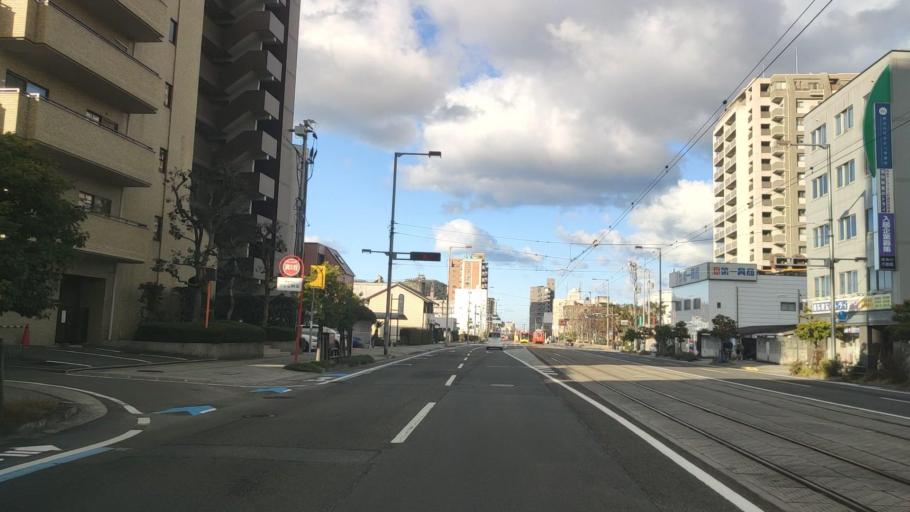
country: JP
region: Ehime
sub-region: Shikoku-chuo Shi
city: Matsuyama
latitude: 33.8474
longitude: 132.7820
